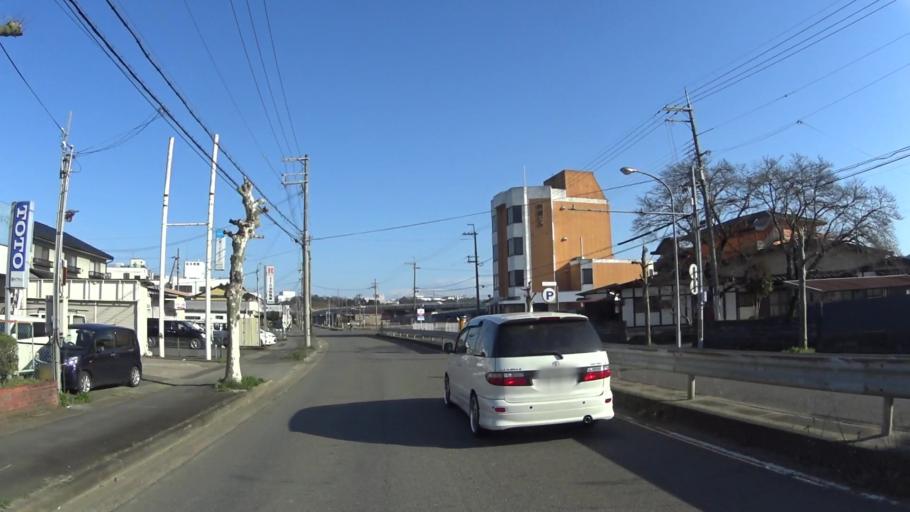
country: JP
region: Kyoto
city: Fukuchiyama
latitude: 35.2927
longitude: 135.1423
